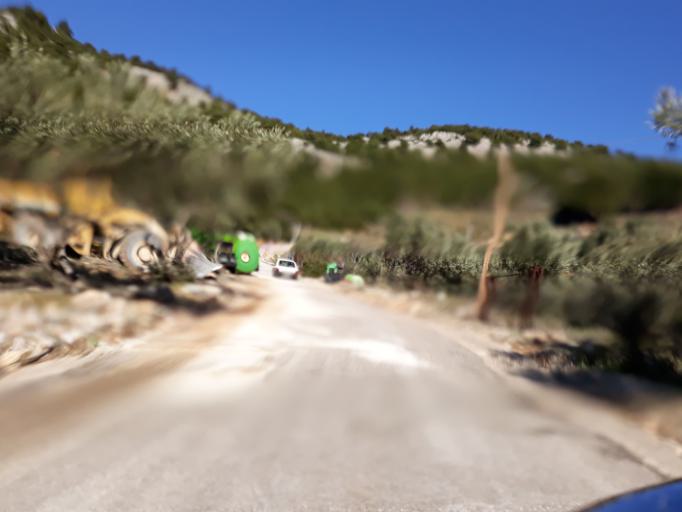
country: GR
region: Attica
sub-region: Nomarchia Dytikis Attikis
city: Fyli
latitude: 38.1141
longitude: 23.6753
